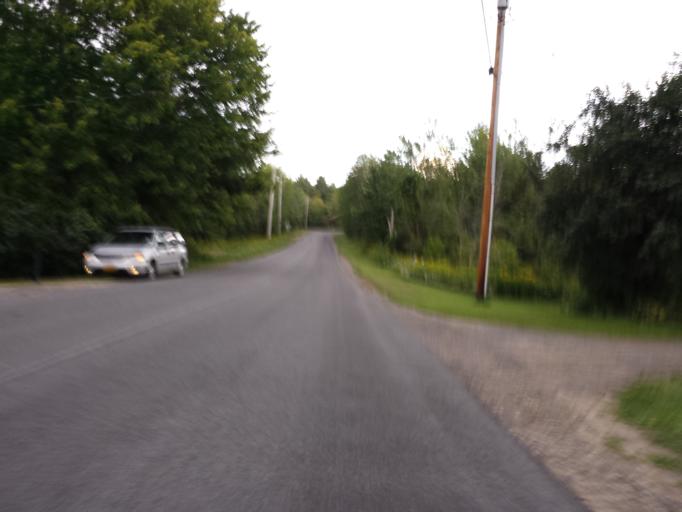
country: US
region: New York
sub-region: St. Lawrence County
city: Potsdam
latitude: 44.6853
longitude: -75.0072
